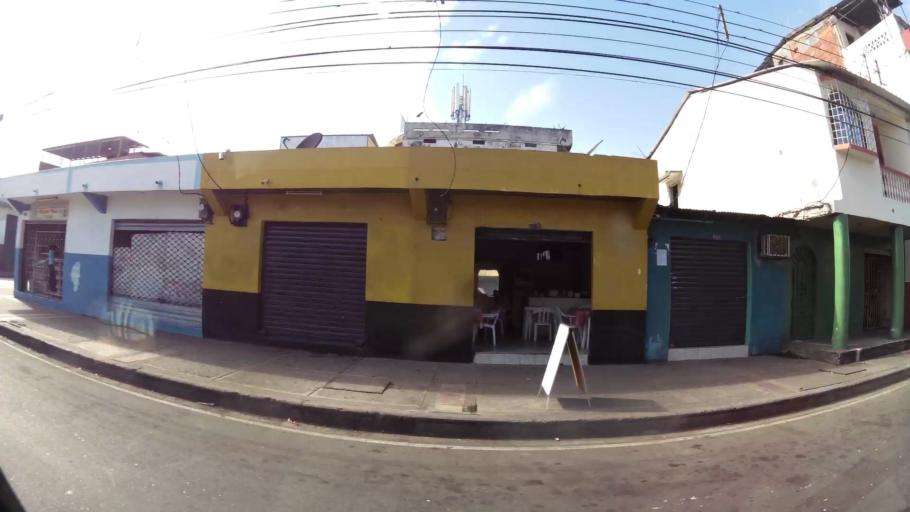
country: EC
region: Guayas
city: Guayaquil
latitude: -2.2008
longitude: -79.9194
